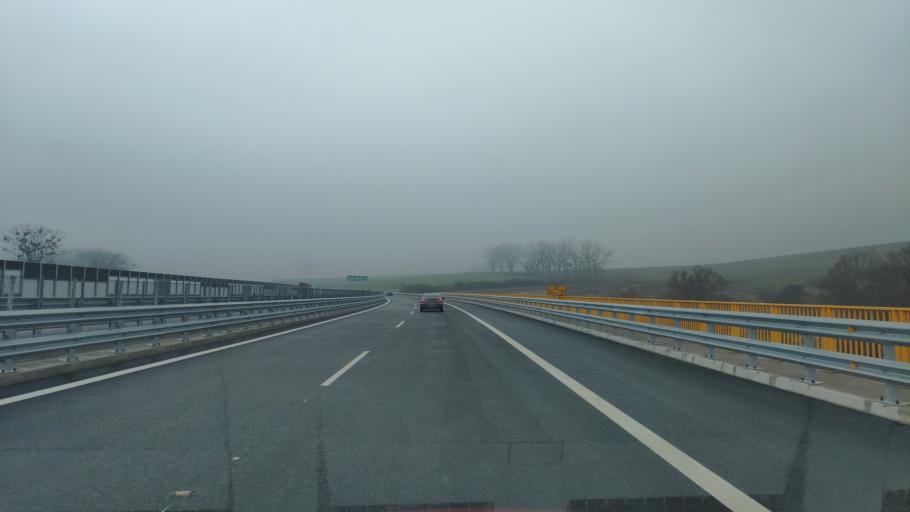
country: SK
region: Kosicky
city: Kosice
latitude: 48.7428
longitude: 21.3647
